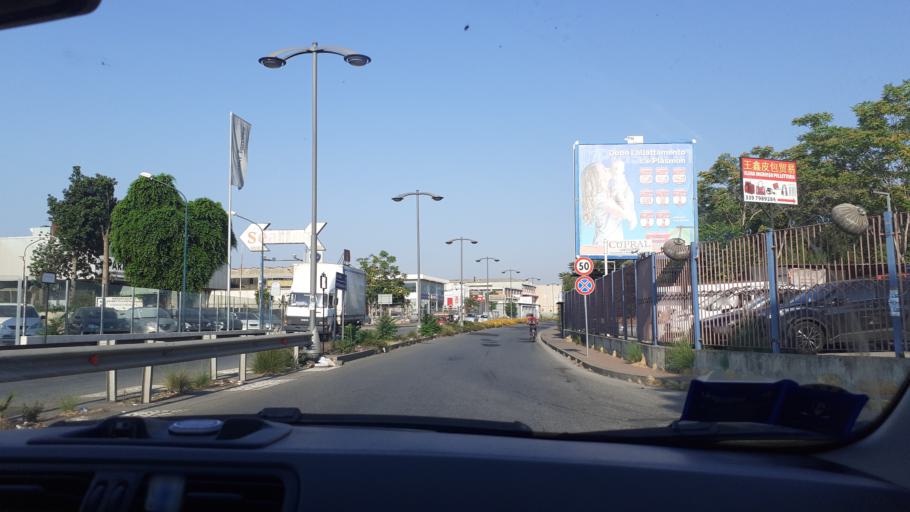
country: IT
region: Sicily
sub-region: Catania
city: Misterbianco
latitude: 37.5115
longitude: 15.0342
